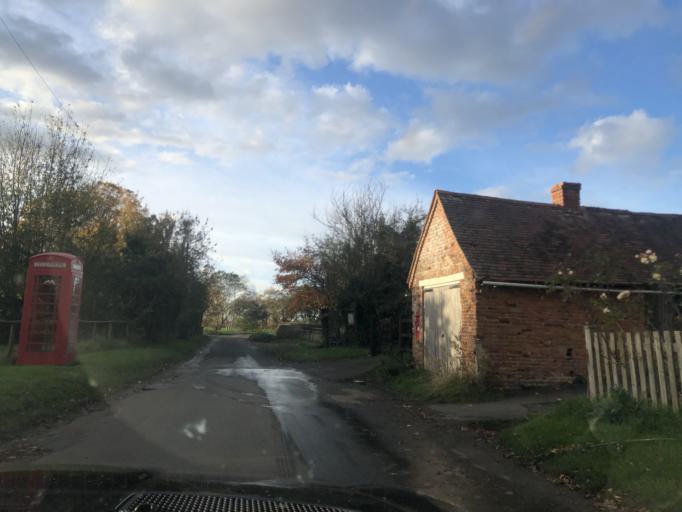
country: GB
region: England
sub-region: Warwickshire
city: Harbury
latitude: 52.2246
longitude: -1.4916
